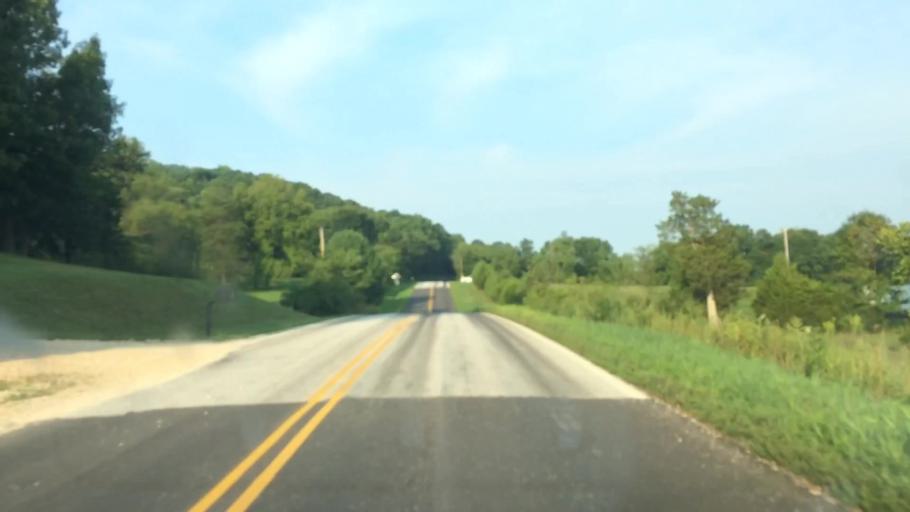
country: US
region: Missouri
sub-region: Greene County
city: Strafford
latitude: 37.1906
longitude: -93.1106
